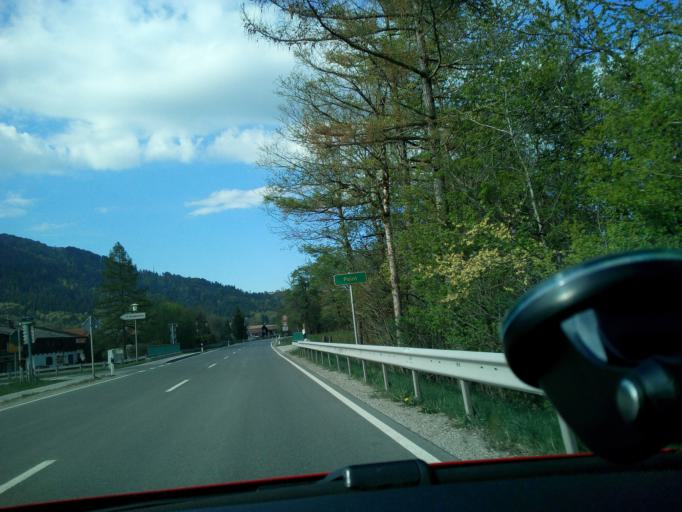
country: DE
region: Bavaria
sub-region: Upper Bavaria
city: Kreuth
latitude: 47.6592
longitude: 11.7494
